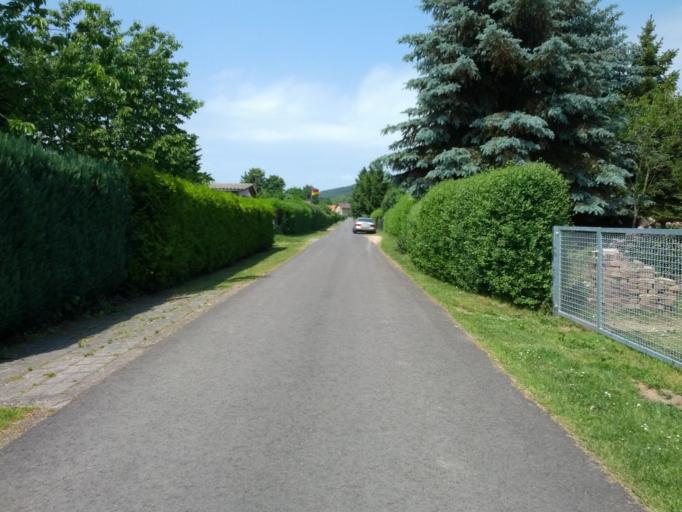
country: DE
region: Thuringia
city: Stadtlengsfeld
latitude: 50.7765
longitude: 10.1333
